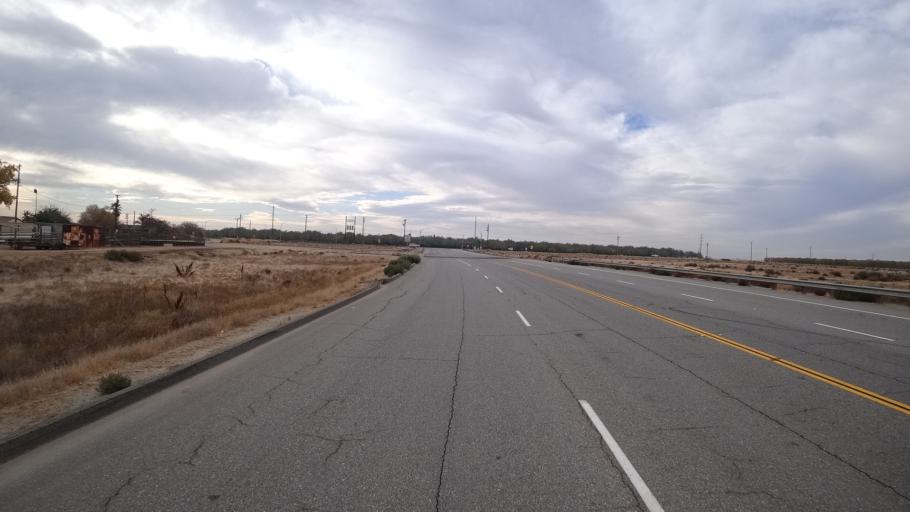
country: US
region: California
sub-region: Kern County
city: Rosedale
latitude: 35.4434
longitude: -119.2044
